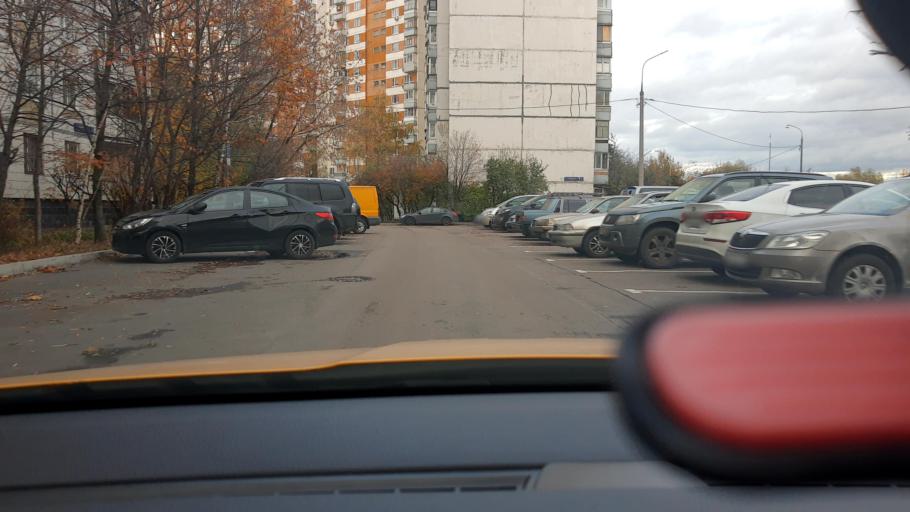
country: RU
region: Moscow
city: Novo-Peredelkino
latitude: 55.6455
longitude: 37.3437
